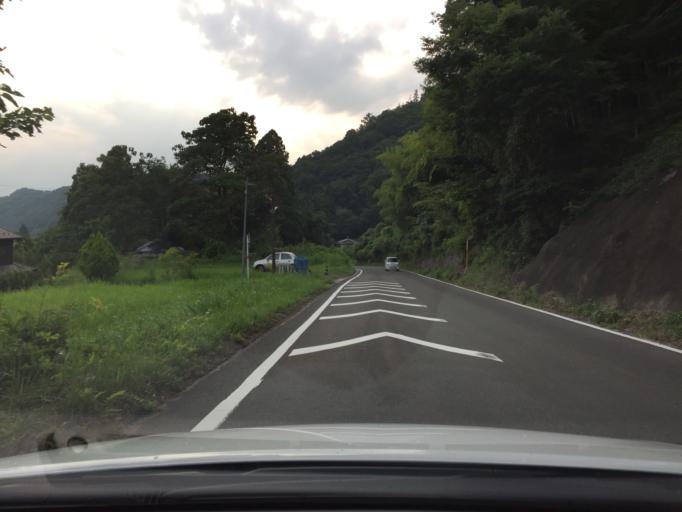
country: JP
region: Fukushima
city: Fukushima-shi
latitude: 37.7211
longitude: 140.4922
